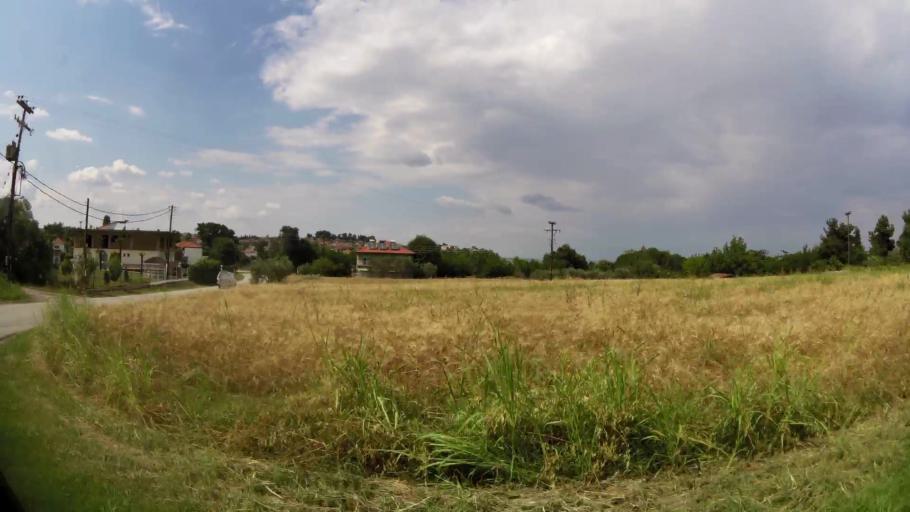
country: GR
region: Central Macedonia
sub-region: Nomos Pierias
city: Makrygialos
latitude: 40.4079
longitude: 22.6088
